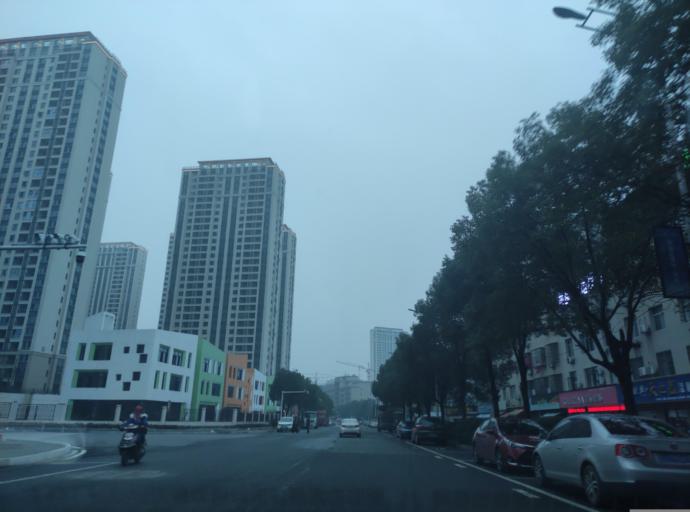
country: CN
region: Jiangxi Sheng
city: Pingxiang
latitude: 27.6666
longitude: 113.8883
